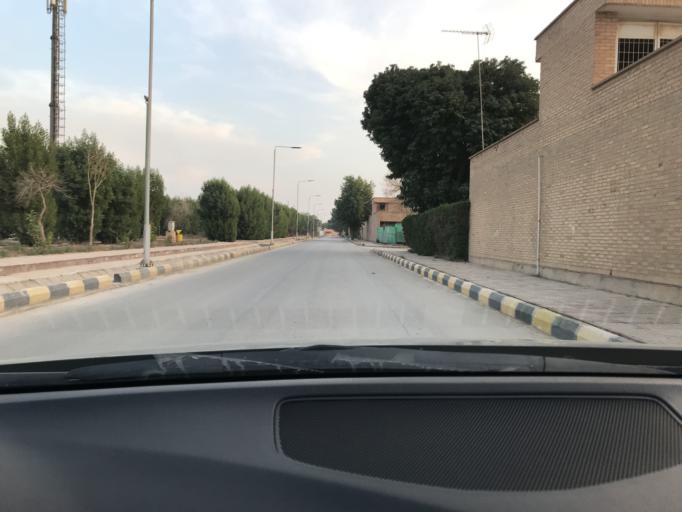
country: IR
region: Khuzestan
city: Ahvaz
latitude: 31.3319
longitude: 48.7346
